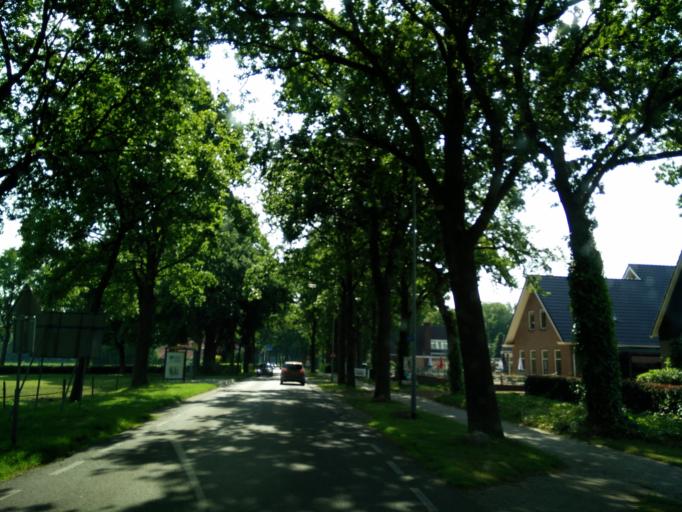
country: NL
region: Drenthe
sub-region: Gemeente Borger-Odoorn
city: Borger
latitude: 52.9755
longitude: 6.7932
